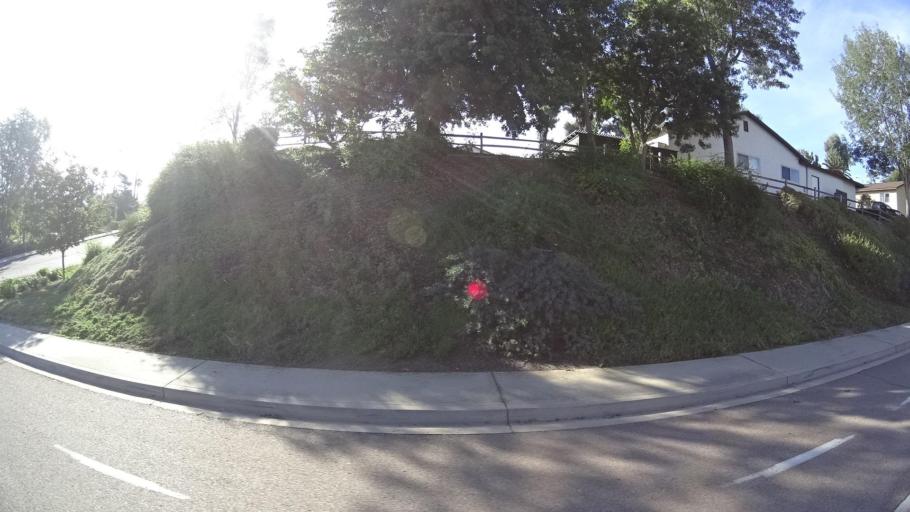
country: US
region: California
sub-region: San Diego County
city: Spring Valley
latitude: 32.7313
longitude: -116.9795
